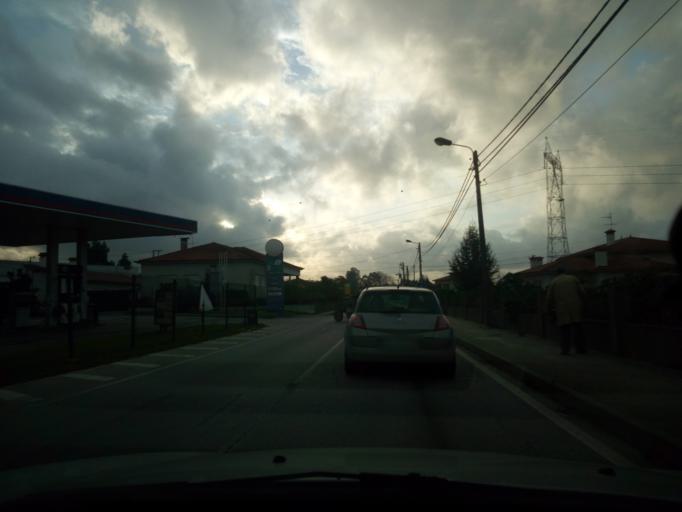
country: PT
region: Aveiro
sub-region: Agueda
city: Agueda
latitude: 40.5583
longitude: -8.4709
